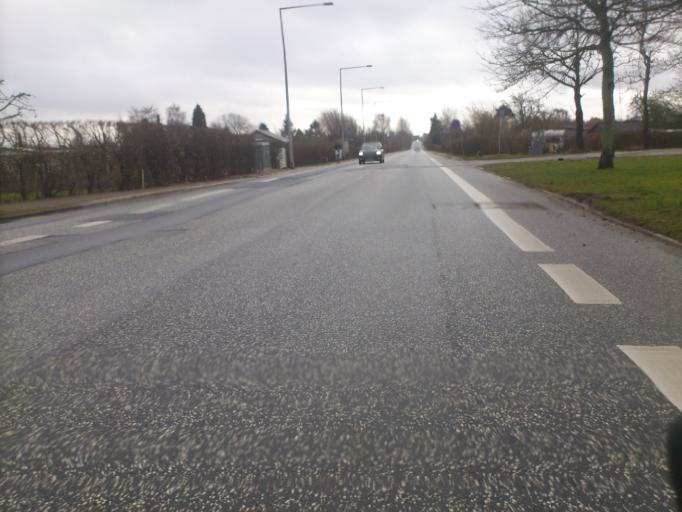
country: DK
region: South Denmark
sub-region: Fredericia Kommune
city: Fredericia
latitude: 55.5871
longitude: 9.7541
